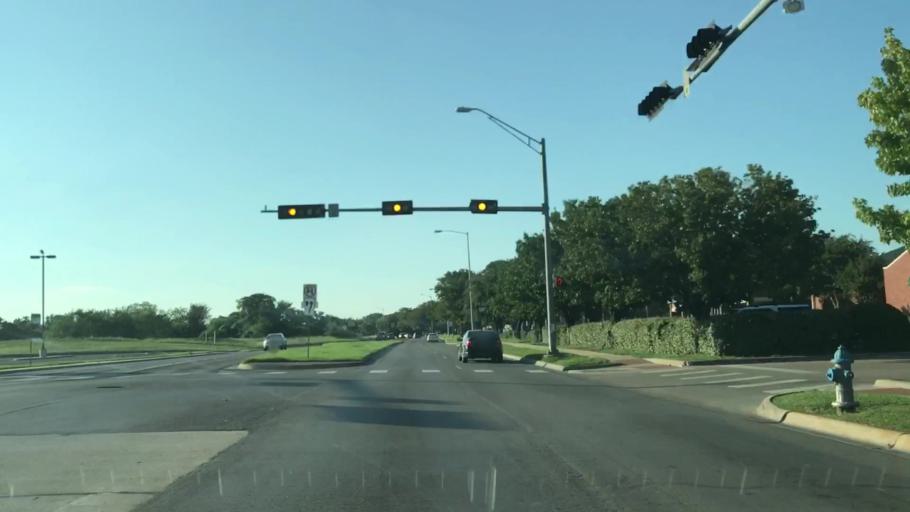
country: US
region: Texas
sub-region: Denton County
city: Denton
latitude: 33.1938
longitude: -97.1063
